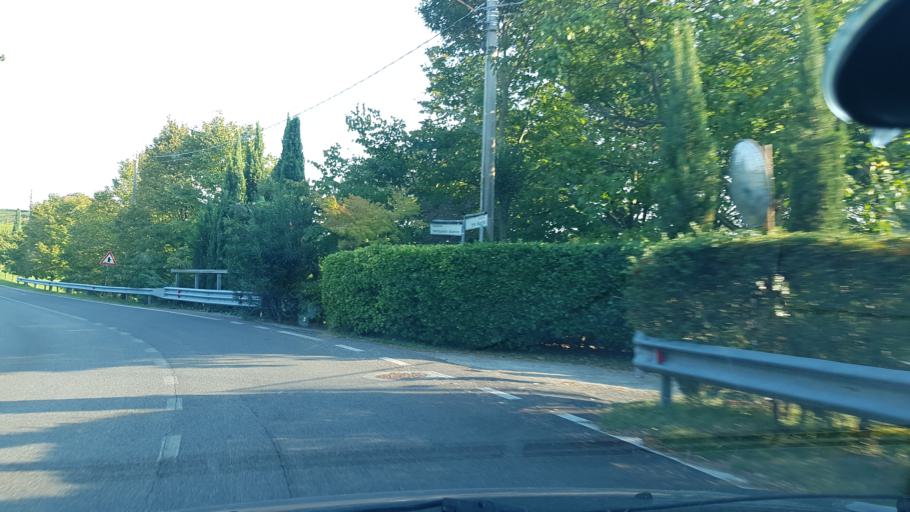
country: IT
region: Friuli Venezia Giulia
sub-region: Provincia di Gorizia
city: San Floriano del Collio
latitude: 45.9835
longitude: 13.6047
